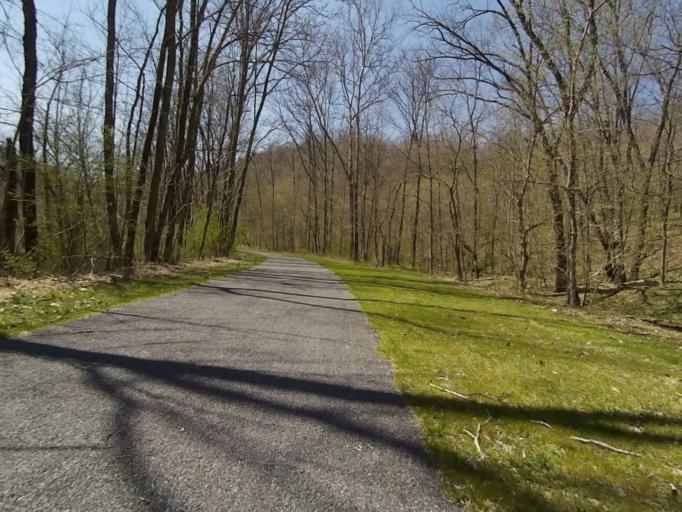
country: US
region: Pennsylvania
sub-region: Blair County
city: Williamsburg
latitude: 40.5468
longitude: -78.1495
